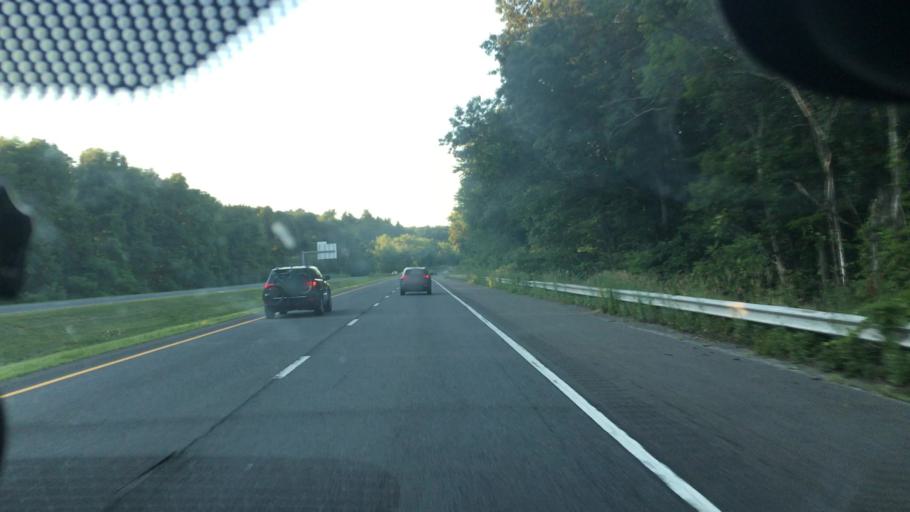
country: US
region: Massachusetts
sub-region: Franklin County
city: Greenfield
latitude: 42.5989
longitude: -72.6164
